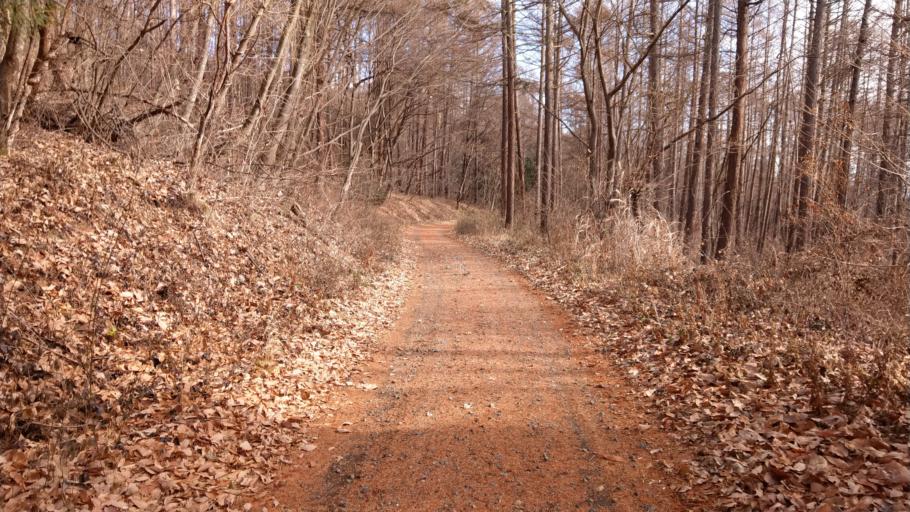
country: JP
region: Nagano
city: Komoro
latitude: 36.3735
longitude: 138.4307
